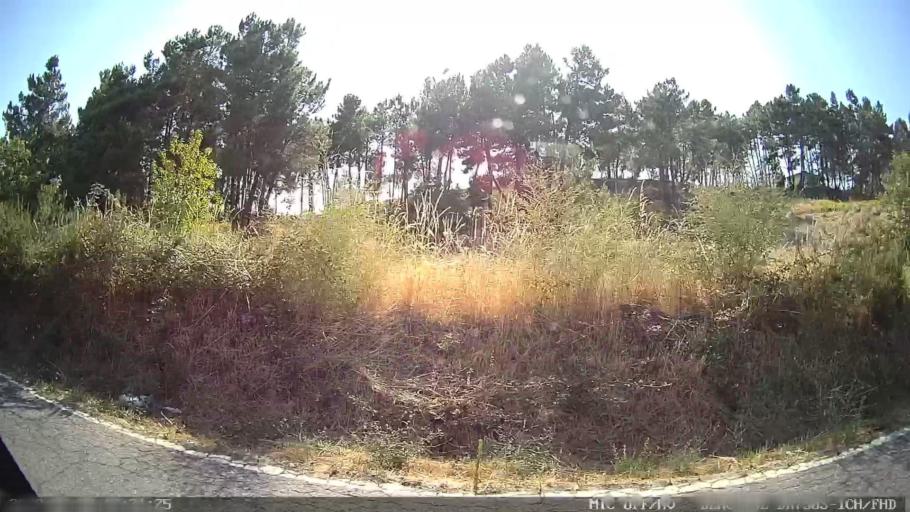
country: PT
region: Vila Real
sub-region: Sabrosa
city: Sabrosa
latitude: 41.2970
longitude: -7.4783
